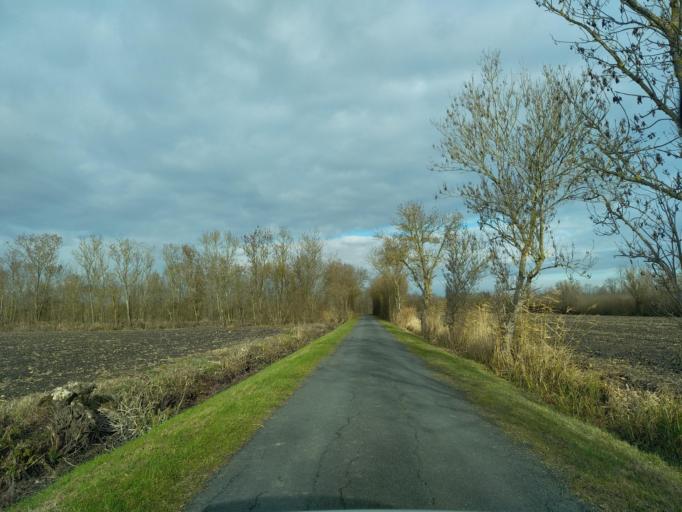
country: FR
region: Pays de la Loire
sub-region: Departement de la Vendee
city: Maillezais
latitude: 46.3271
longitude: -0.7945
